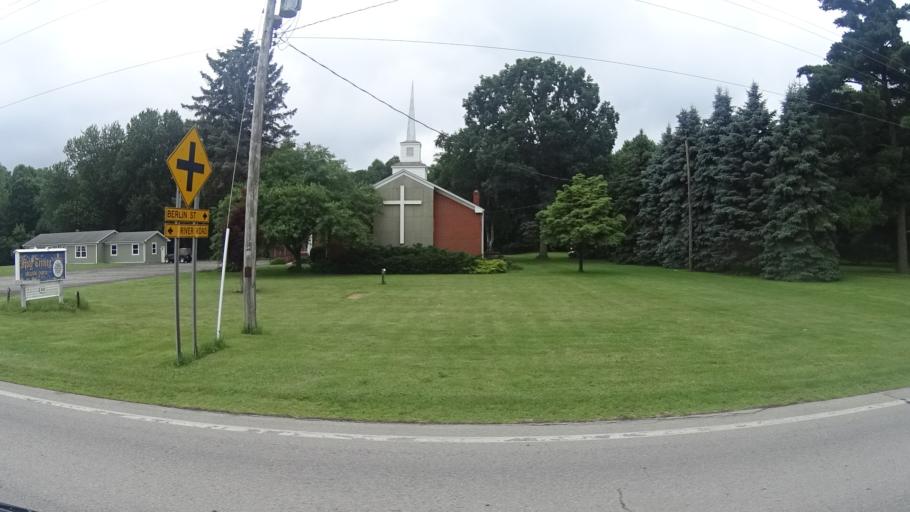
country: US
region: Ohio
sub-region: Erie County
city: Milan
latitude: 41.2991
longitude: -82.5921
